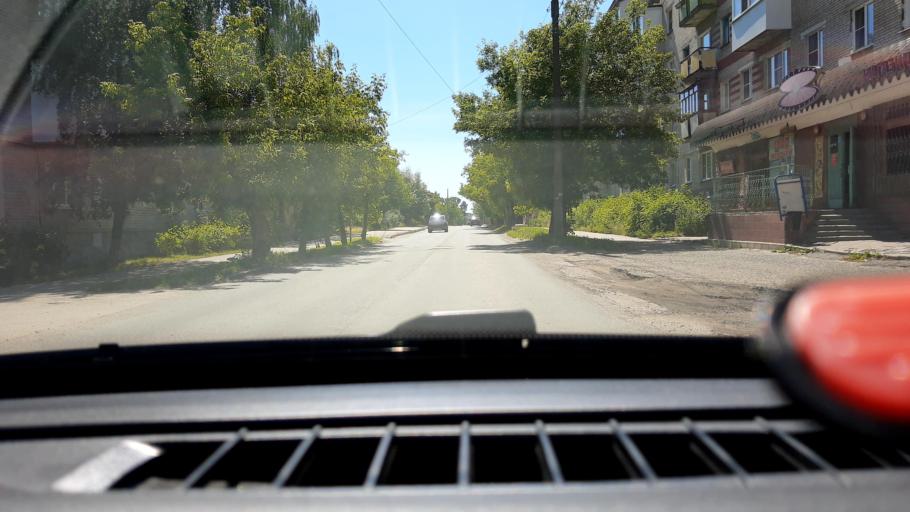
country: RU
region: Nizjnij Novgorod
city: Dzerzhinsk
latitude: 56.2516
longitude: 43.4738
